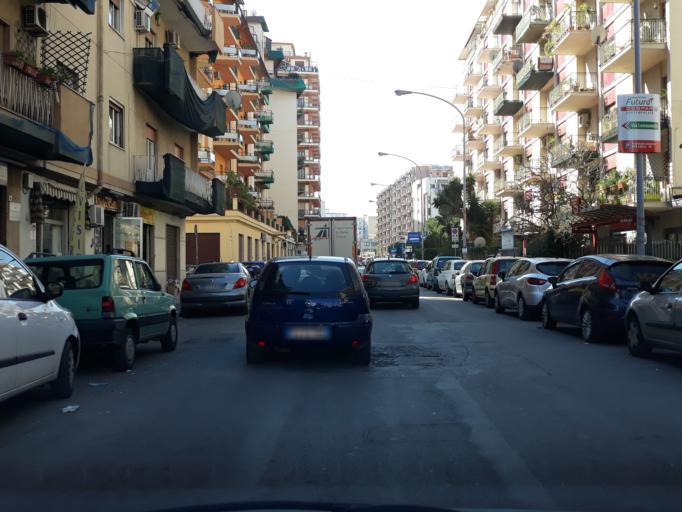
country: IT
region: Sicily
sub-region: Palermo
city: Palermo
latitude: 38.1303
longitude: 13.3380
